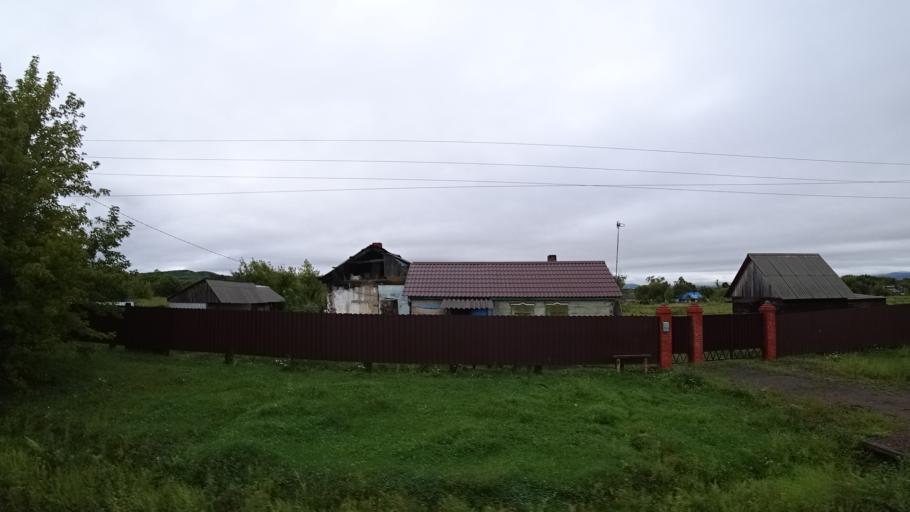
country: RU
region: Primorskiy
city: Monastyrishche
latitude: 44.2590
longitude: 132.4236
